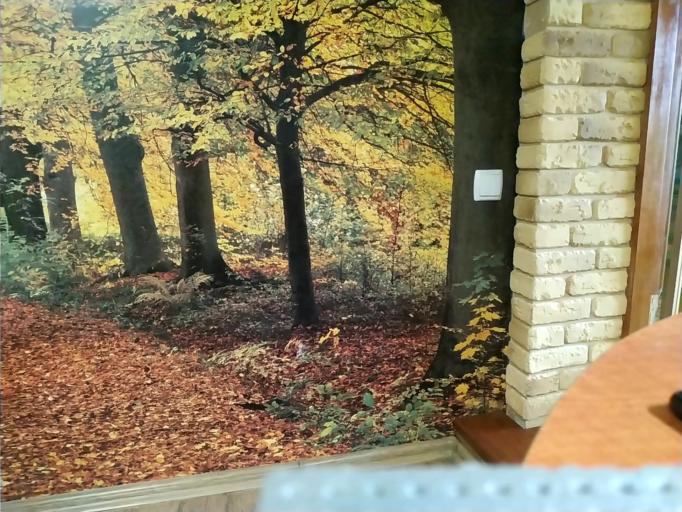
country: RU
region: Vladimir
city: Bavleny
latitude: 56.3702
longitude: 39.6062
